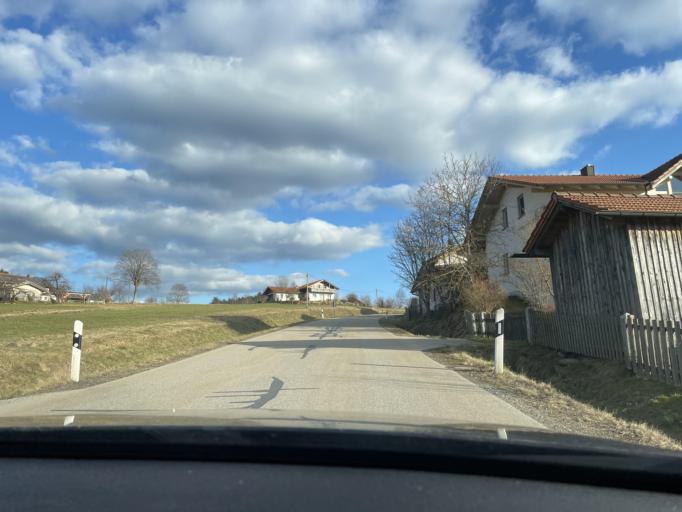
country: DE
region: Bavaria
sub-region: Lower Bavaria
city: Kollnburg
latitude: 49.0522
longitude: 12.8577
